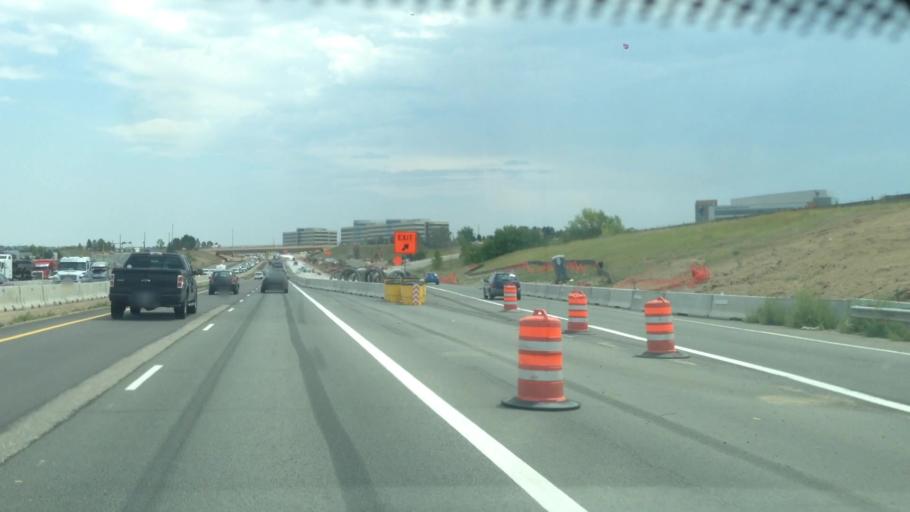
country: US
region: Colorado
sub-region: Arapahoe County
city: Columbine Valley
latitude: 39.5620
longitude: -105.0150
